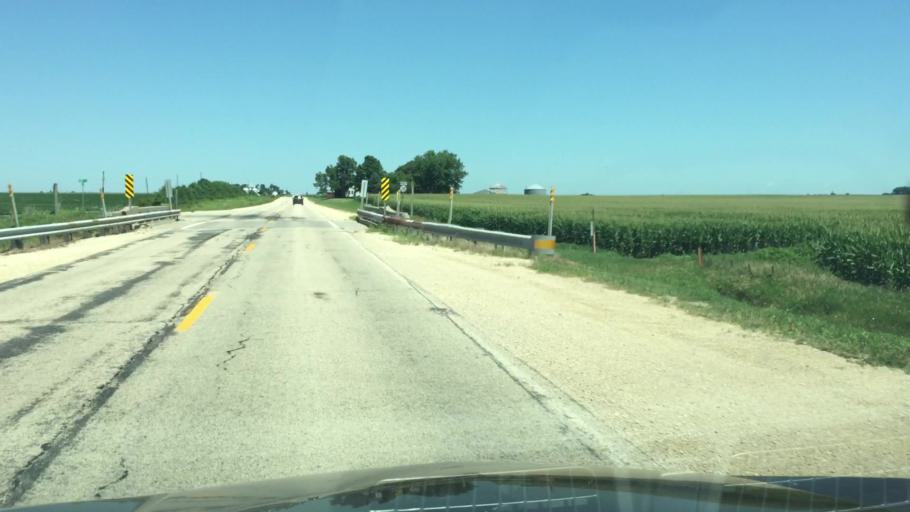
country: US
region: Iowa
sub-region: Cedar County
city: Mechanicsville
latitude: 41.9026
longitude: -91.1520
